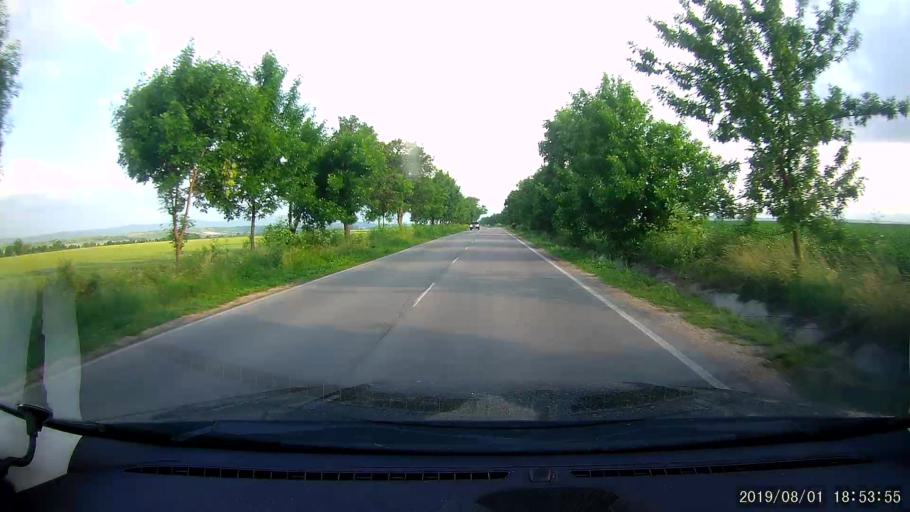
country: BG
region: Shumen
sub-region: Obshtina Shumen
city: Shumen
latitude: 43.2118
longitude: 26.9983
